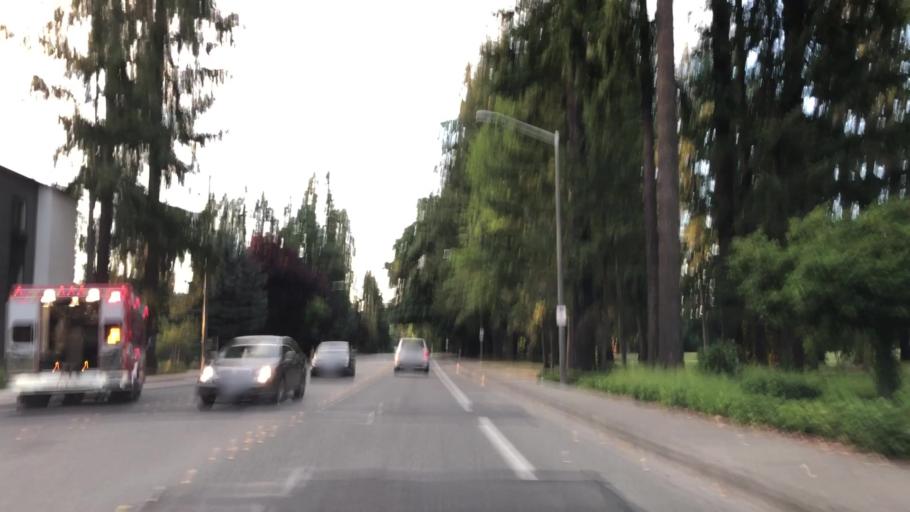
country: US
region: Washington
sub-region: King County
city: Redmond
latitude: 47.6686
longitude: -122.1001
